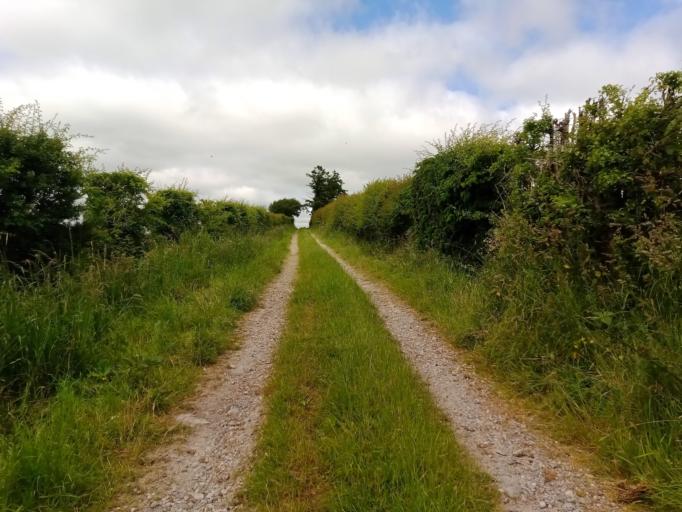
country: IE
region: Leinster
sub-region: Kilkenny
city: Ballyragget
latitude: 52.7931
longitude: -7.4564
